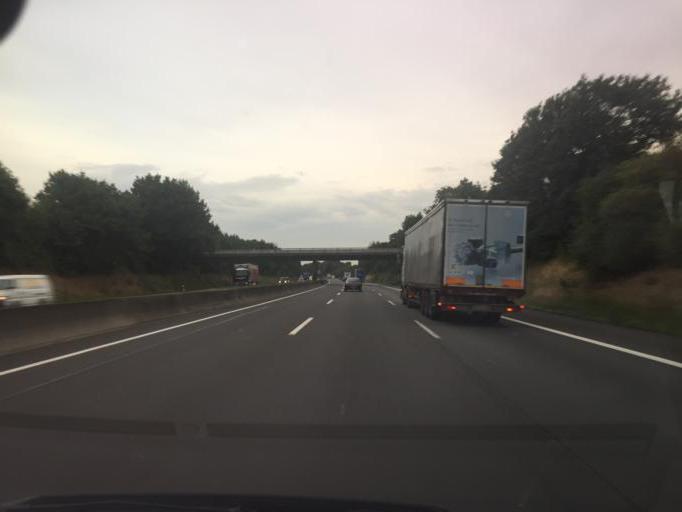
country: DE
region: North Rhine-Westphalia
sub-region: Regierungsbezirk Koln
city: Titz
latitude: 51.0763
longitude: 6.4261
